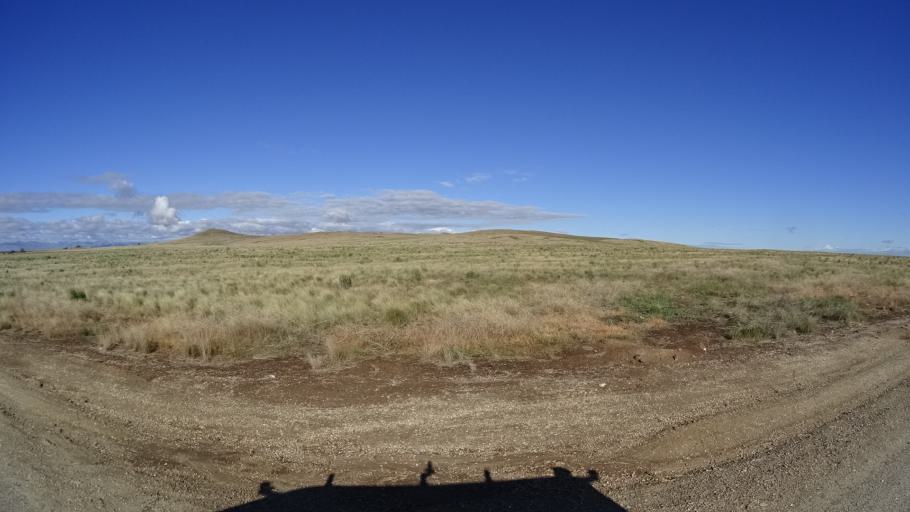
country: US
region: Idaho
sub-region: Ada County
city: Kuna
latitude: 43.4418
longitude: -116.4140
